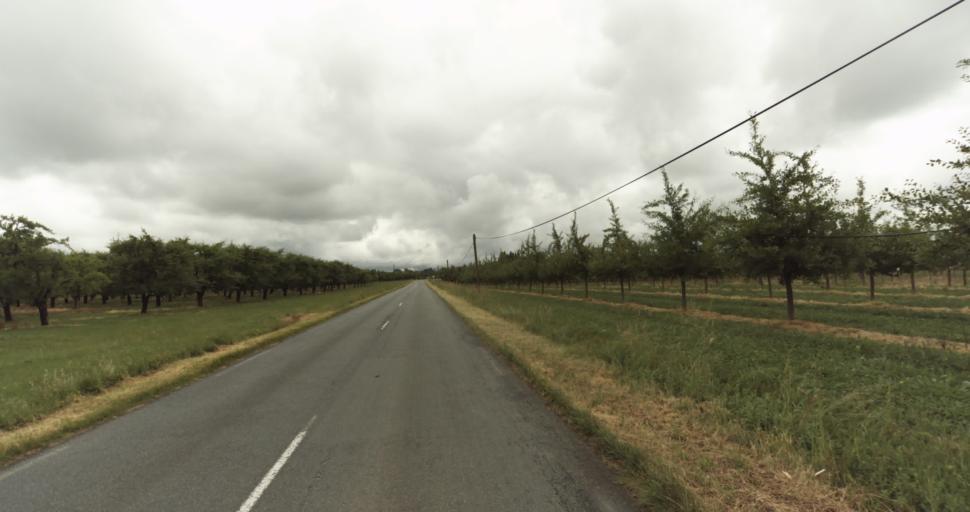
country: FR
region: Aquitaine
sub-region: Departement de la Dordogne
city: Beaumont-du-Perigord
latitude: 44.7348
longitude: 0.7850
